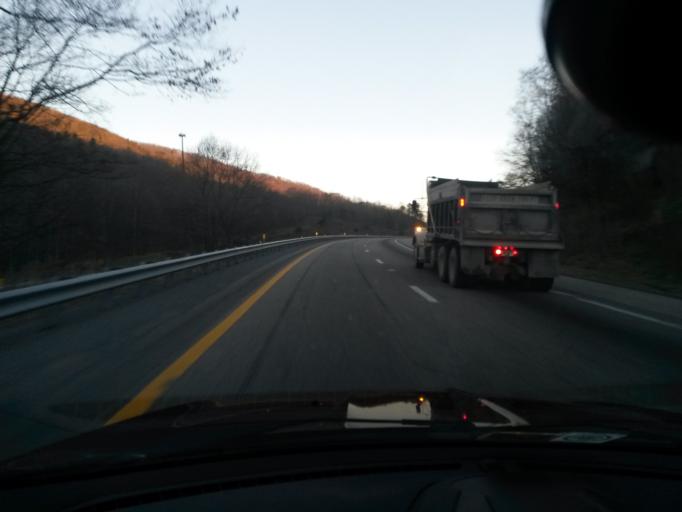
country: US
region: Virginia
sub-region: City of Lexington
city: Lexington
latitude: 37.8676
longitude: -79.6238
